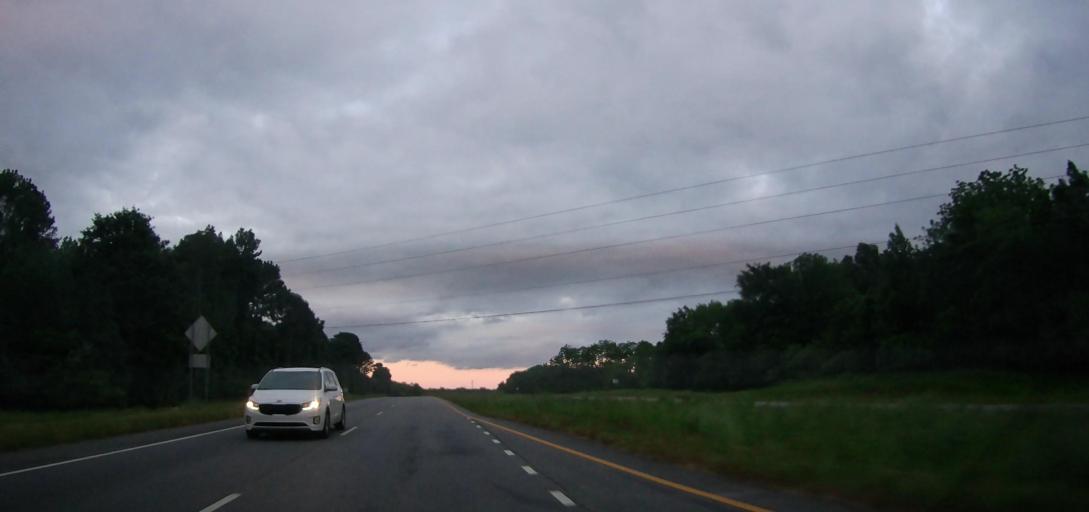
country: US
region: Georgia
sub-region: Jackson County
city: Arcade
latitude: 34.0655
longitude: -83.5419
